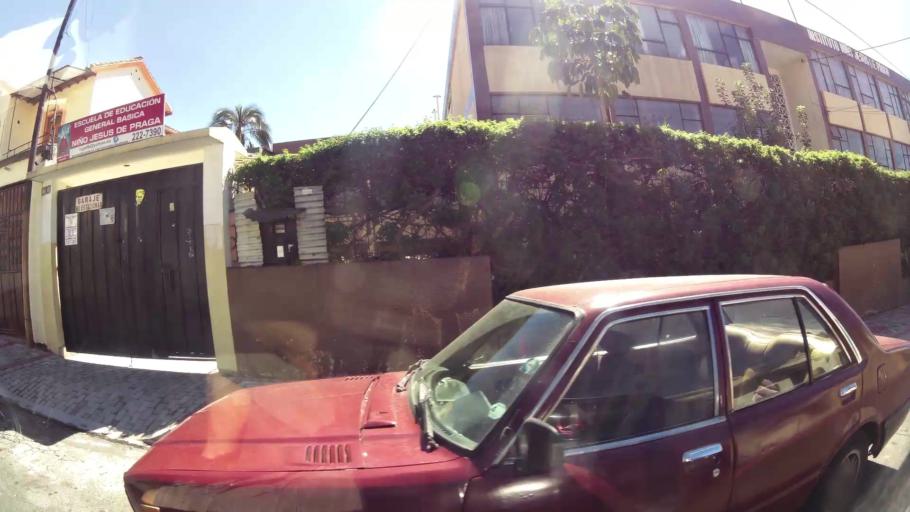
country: EC
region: Pichincha
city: Quito
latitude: -0.1965
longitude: -78.4967
